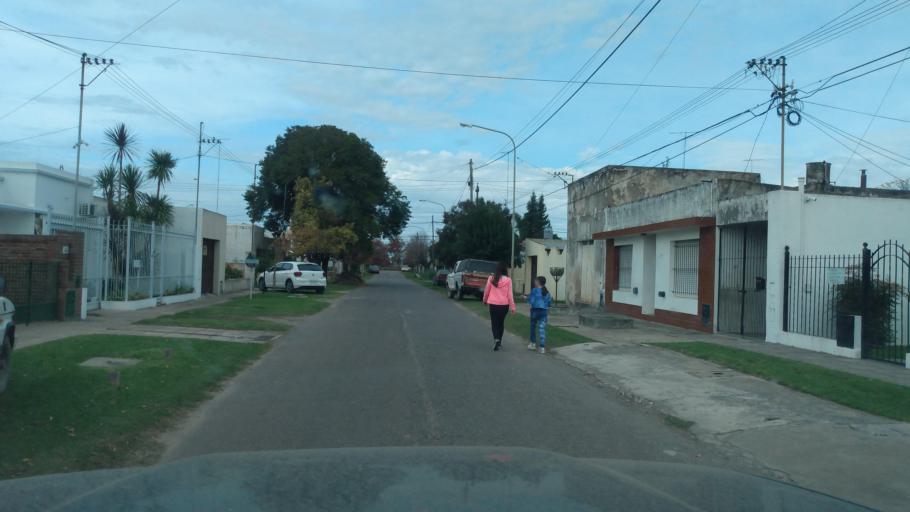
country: AR
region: Buenos Aires
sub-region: Partido de Lujan
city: Lujan
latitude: -34.6022
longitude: -59.1746
